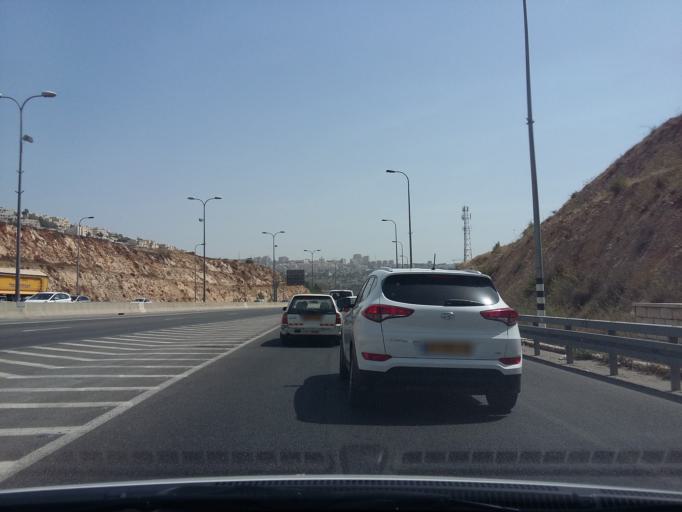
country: PS
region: West Bank
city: Bir Nabala
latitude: 31.8220
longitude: 35.2140
